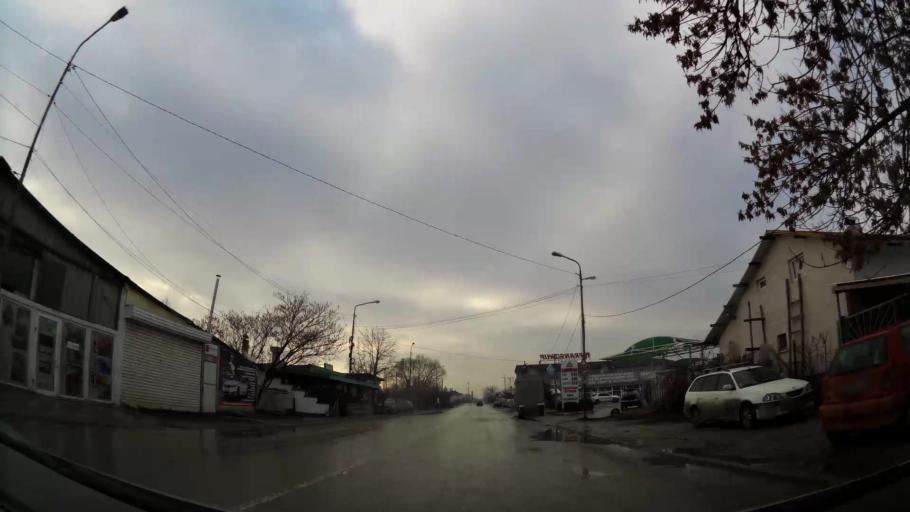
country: BG
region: Sofia-Capital
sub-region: Stolichna Obshtina
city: Sofia
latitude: 42.7346
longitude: 23.3432
